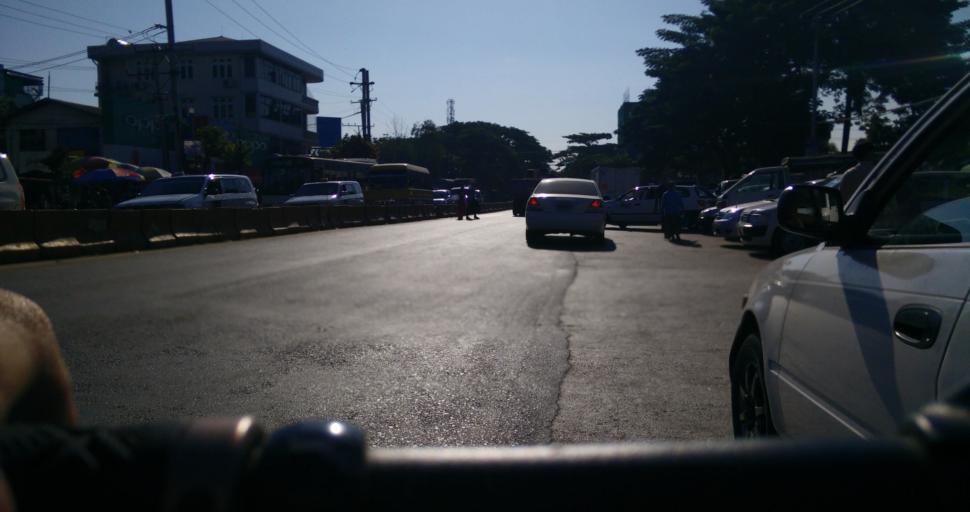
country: MM
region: Yangon
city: Yangon
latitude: 16.8429
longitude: 96.2042
